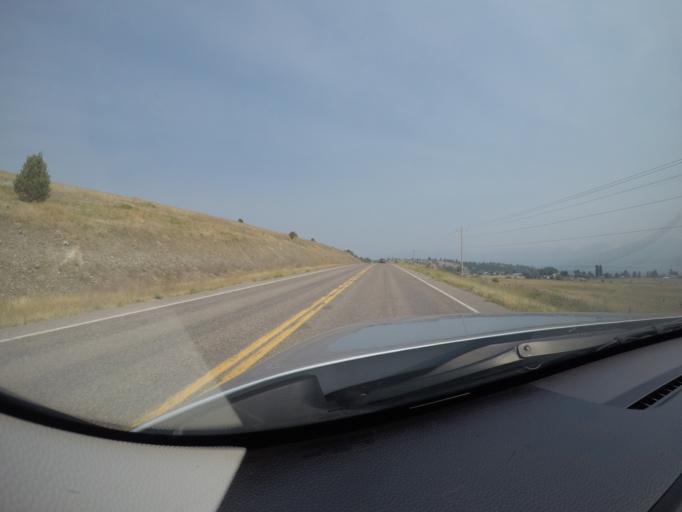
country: US
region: Montana
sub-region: Lake County
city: Polson
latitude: 47.7365
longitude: -114.1851
